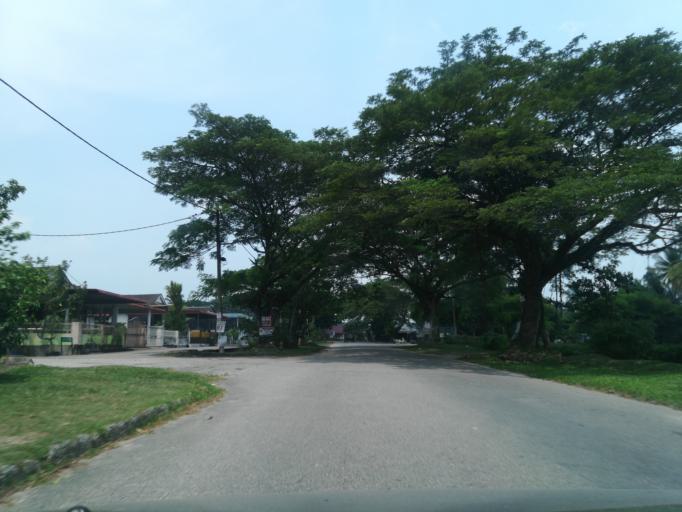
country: MY
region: Kedah
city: Kulim
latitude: 5.4014
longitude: 100.5627
